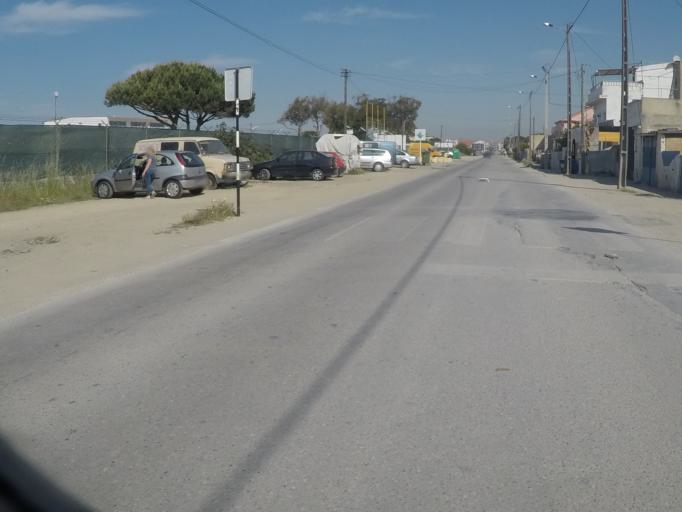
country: PT
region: Setubal
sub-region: Almada
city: Costa de Caparica
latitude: 38.6328
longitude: -9.2249
